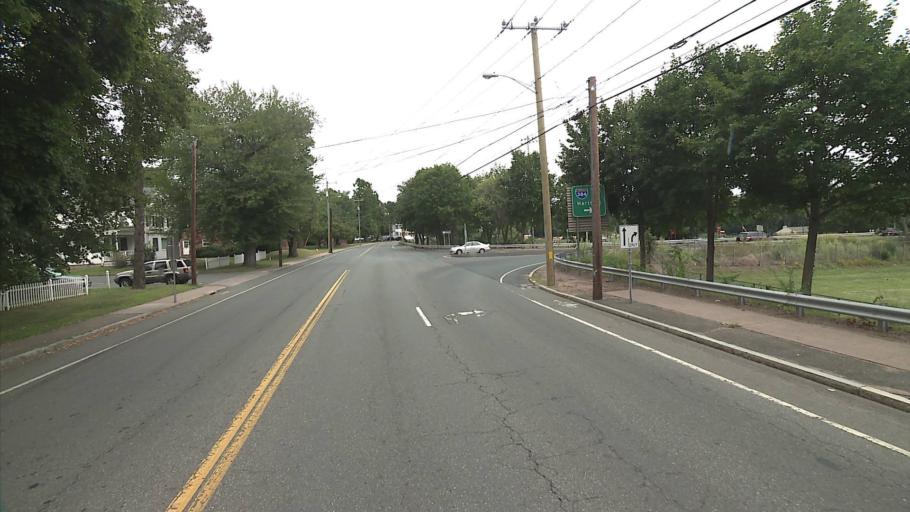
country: US
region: Connecticut
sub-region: Hartford County
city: Manchester
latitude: 41.7648
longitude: -72.5184
